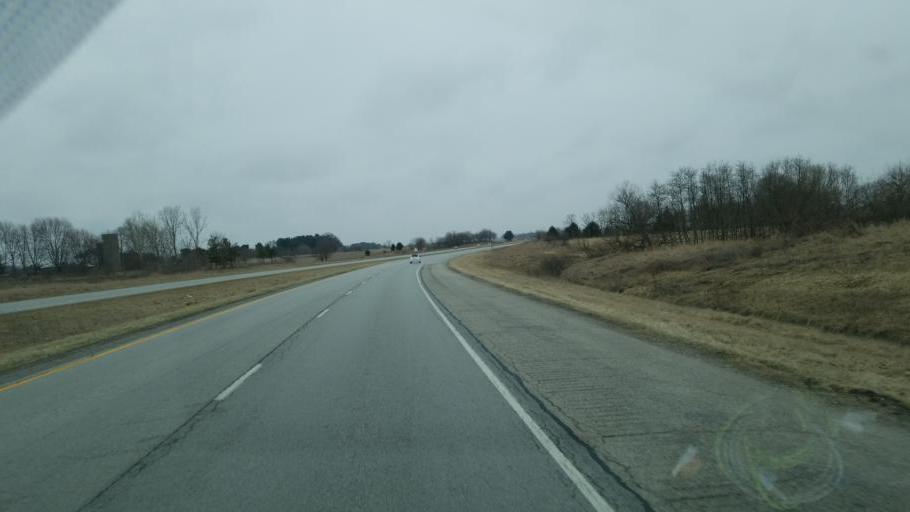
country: US
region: Indiana
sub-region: Fulton County
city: Rochester
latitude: 40.9191
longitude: -86.1605
